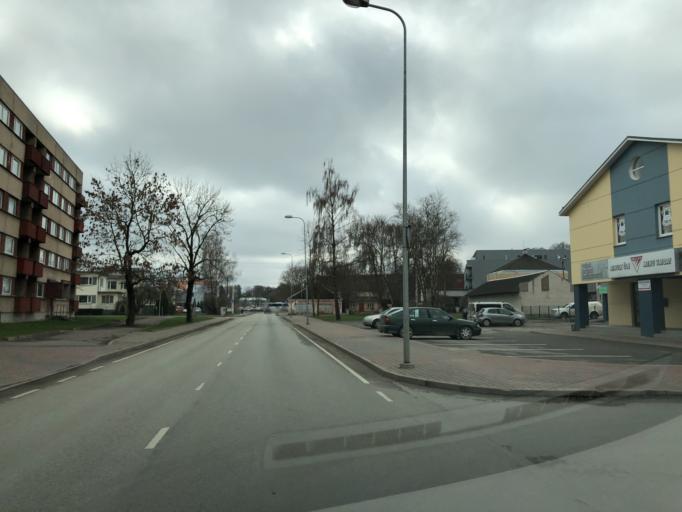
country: EE
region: Laeaene-Virumaa
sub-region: Rakvere linn
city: Rakvere
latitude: 59.3499
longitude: 26.3565
